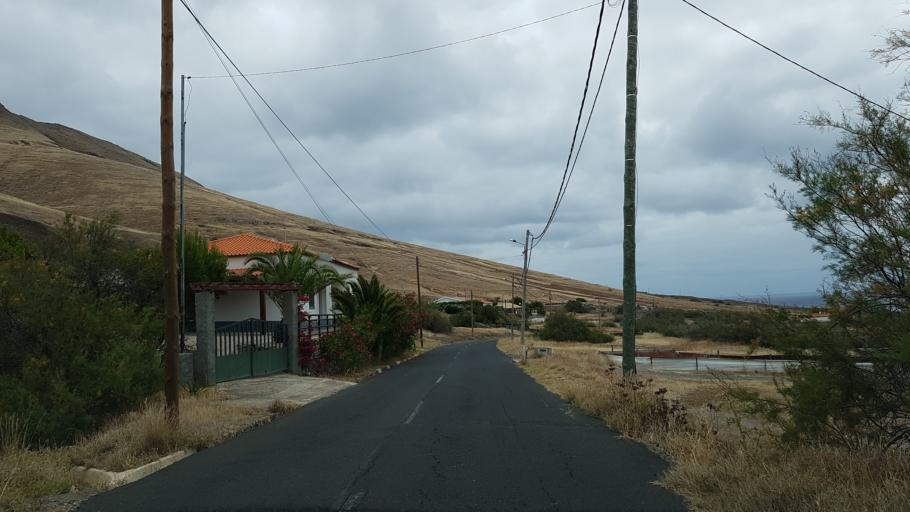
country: PT
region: Madeira
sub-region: Porto Santo
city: Vila de Porto Santo
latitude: 33.0723
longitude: -16.3069
